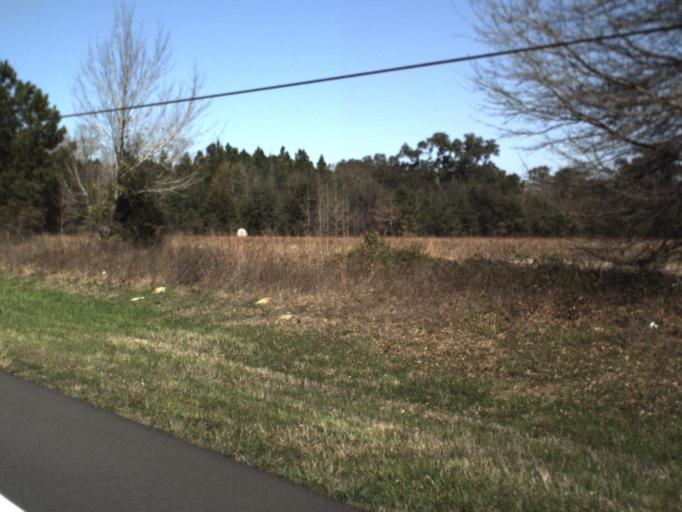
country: US
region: Florida
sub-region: Jackson County
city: Sneads
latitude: 30.7988
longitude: -85.0298
